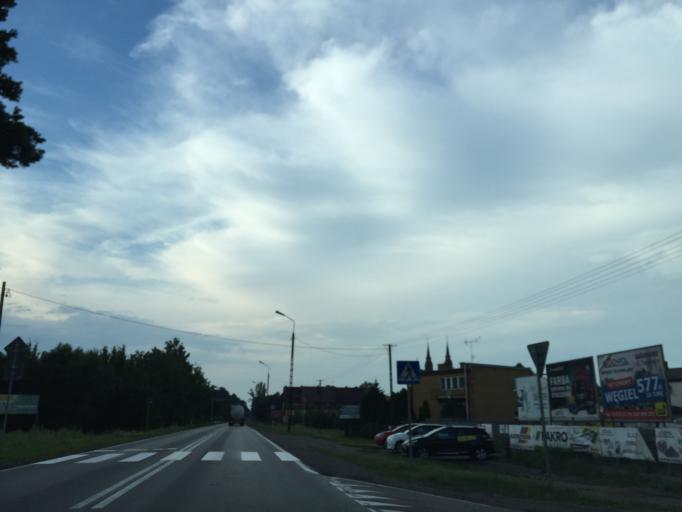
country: PL
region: Masovian Voivodeship
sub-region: Powiat wegrowski
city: Sadowne
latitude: 52.6375
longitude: 21.8450
